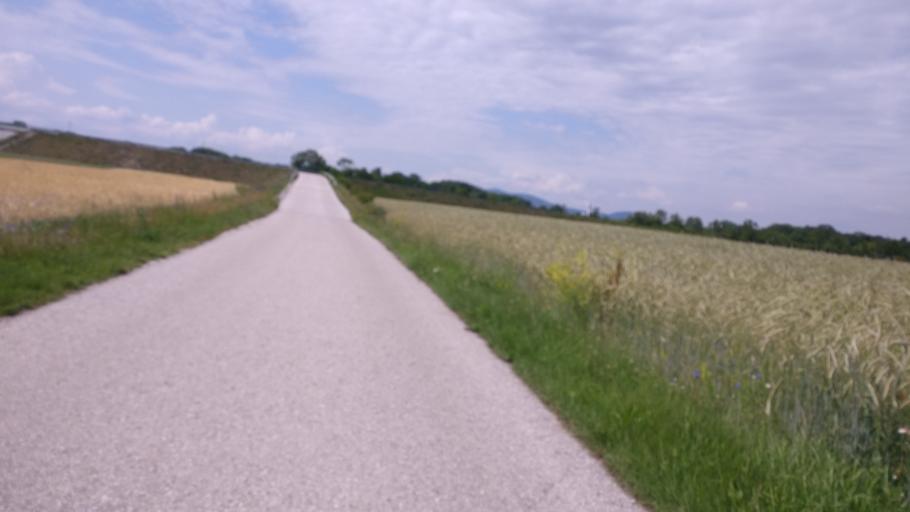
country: AT
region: Lower Austria
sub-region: Politischer Bezirk Wiener Neustadt
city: Sollenau
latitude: 47.9016
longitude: 16.2682
